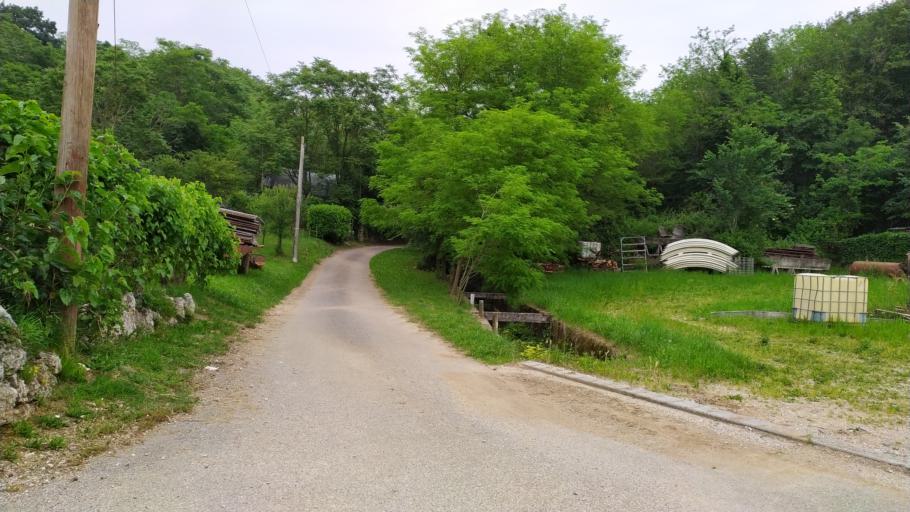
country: IT
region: Friuli Venezia Giulia
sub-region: Provincia di Udine
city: San Daniele del Friuli
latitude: 46.1812
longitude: 13.0288
